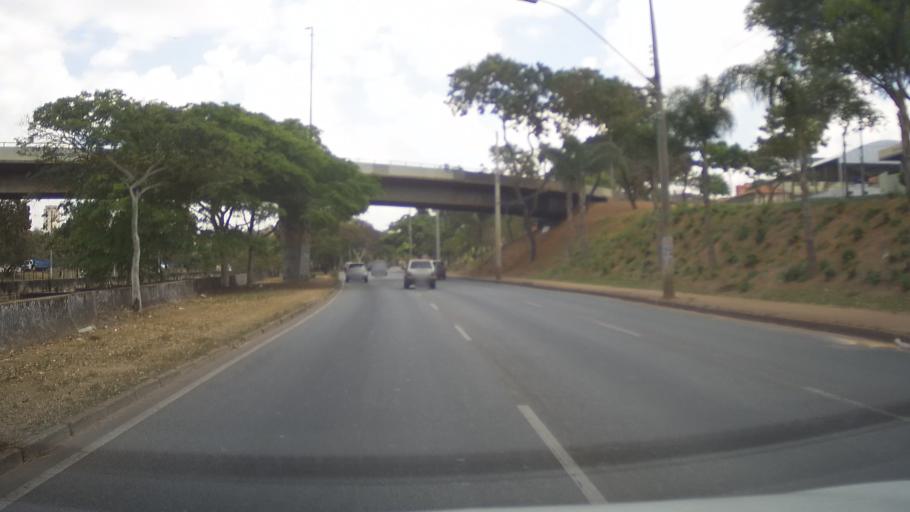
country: BR
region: Minas Gerais
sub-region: Belo Horizonte
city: Belo Horizonte
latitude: -19.9232
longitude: -43.9761
